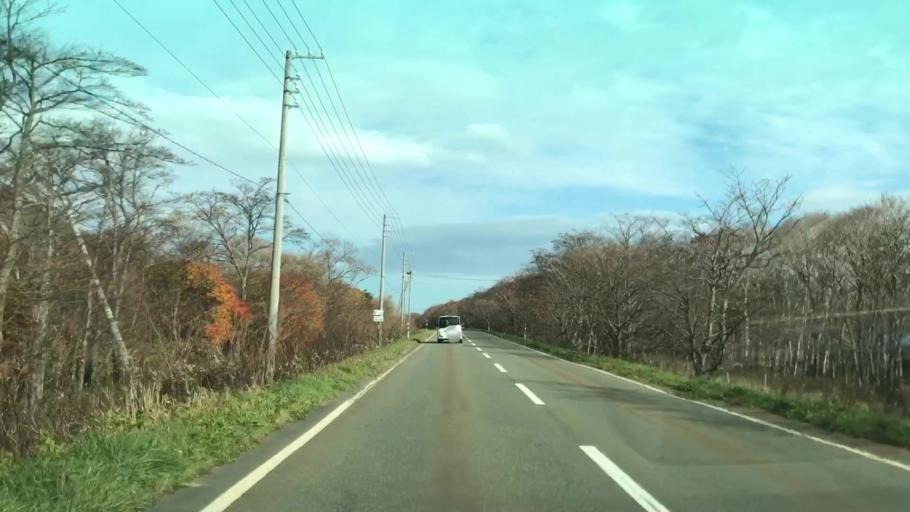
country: JP
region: Hokkaido
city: Obihiro
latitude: 42.0235
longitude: 143.2636
